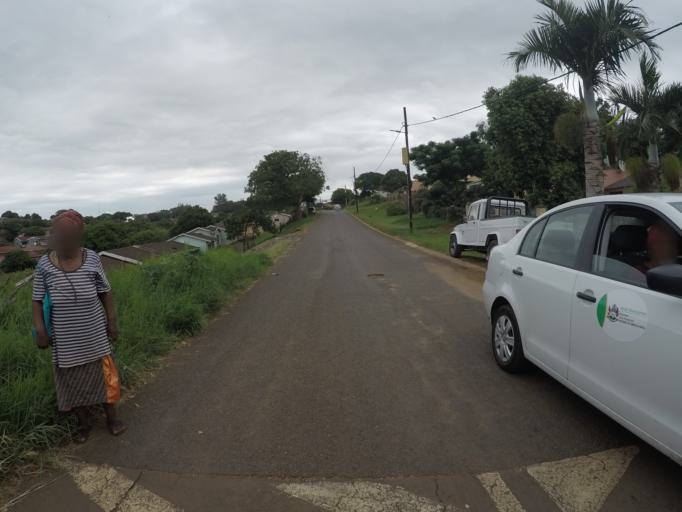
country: ZA
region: KwaZulu-Natal
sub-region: uThungulu District Municipality
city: Empangeni
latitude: -28.7717
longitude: 31.8676
